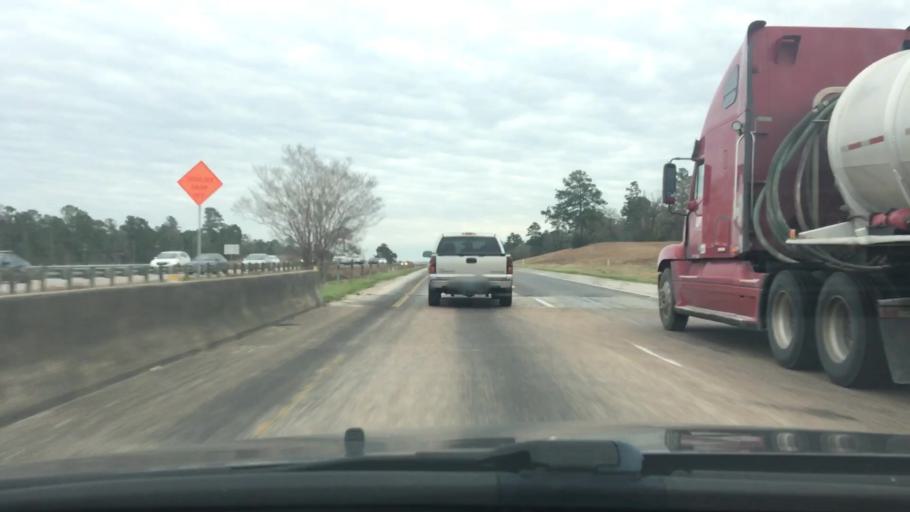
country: US
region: Texas
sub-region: Walker County
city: Huntsville
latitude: 30.7764
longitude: -95.6501
